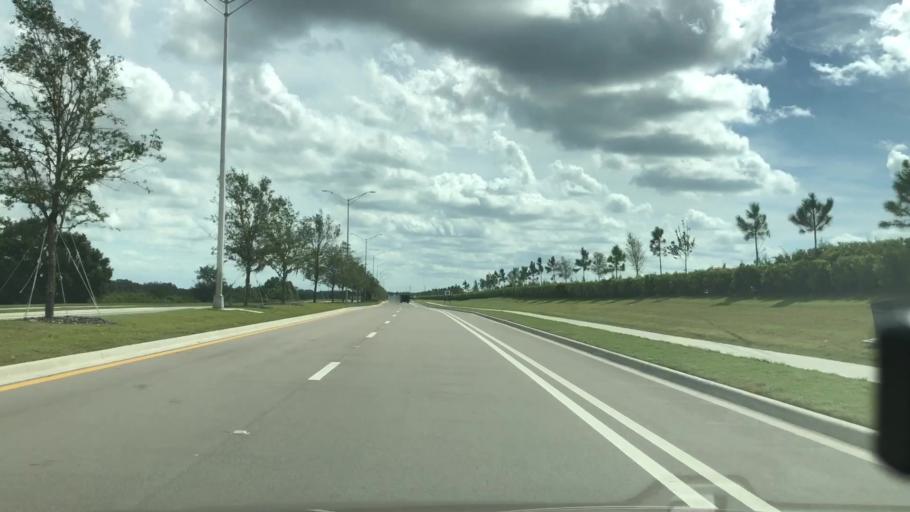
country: US
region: Florida
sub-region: Sarasota County
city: The Meadows
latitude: 27.3702
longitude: -82.3953
